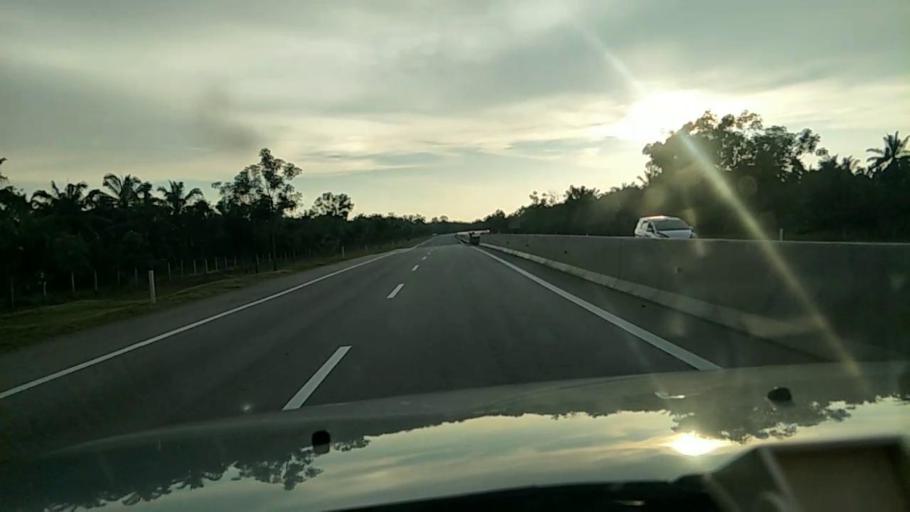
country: MY
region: Selangor
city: Batu Arang
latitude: 3.2880
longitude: 101.4232
